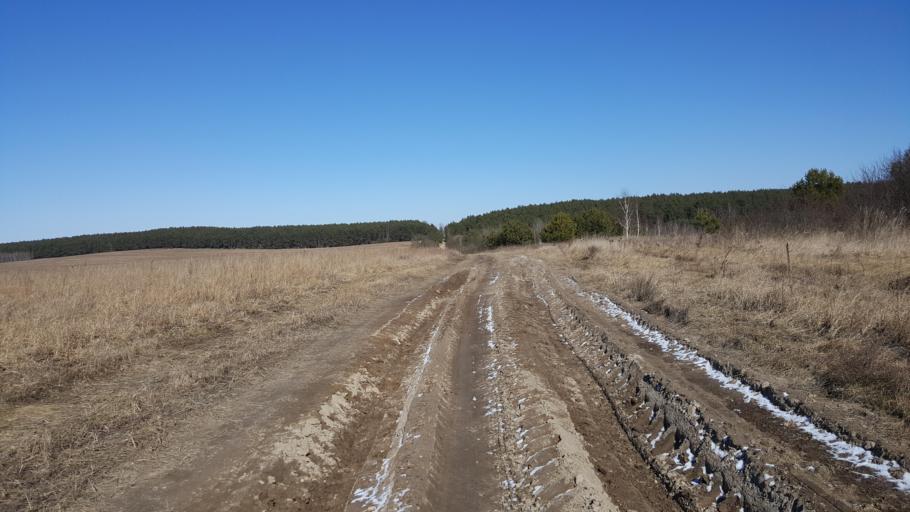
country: BY
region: Brest
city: Kamyanyets
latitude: 52.3738
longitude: 23.8364
